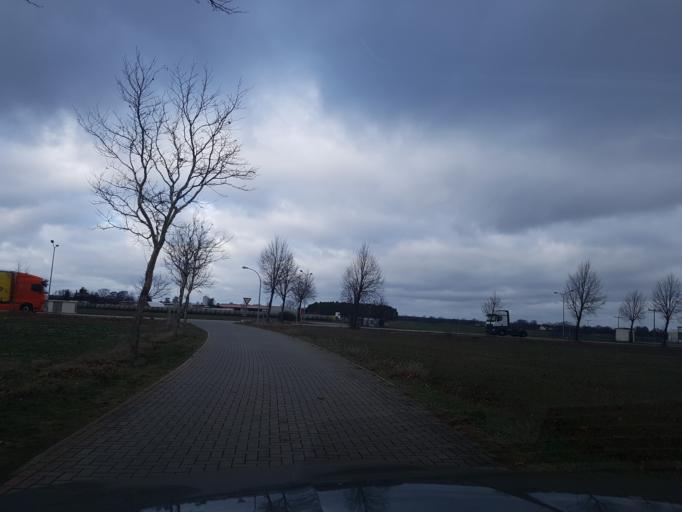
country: DE
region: Brandenburg
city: Falkenberg
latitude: 51.5979
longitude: 13.3008
